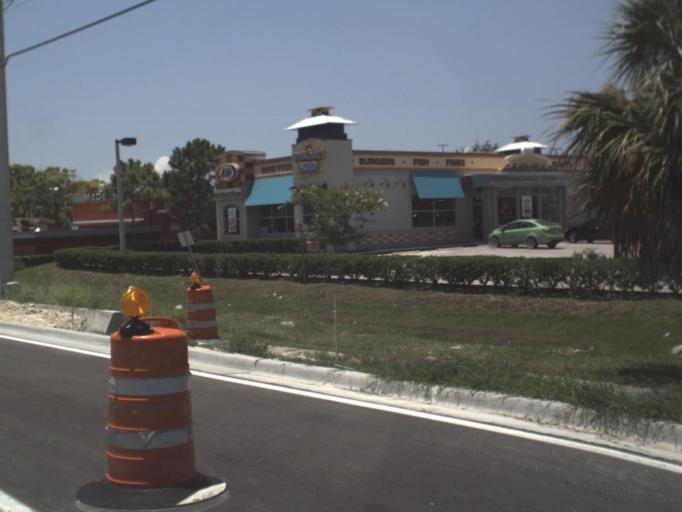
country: US
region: Florida
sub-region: Pasco County
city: Port Richey
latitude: 28.2821
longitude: -82.7165
